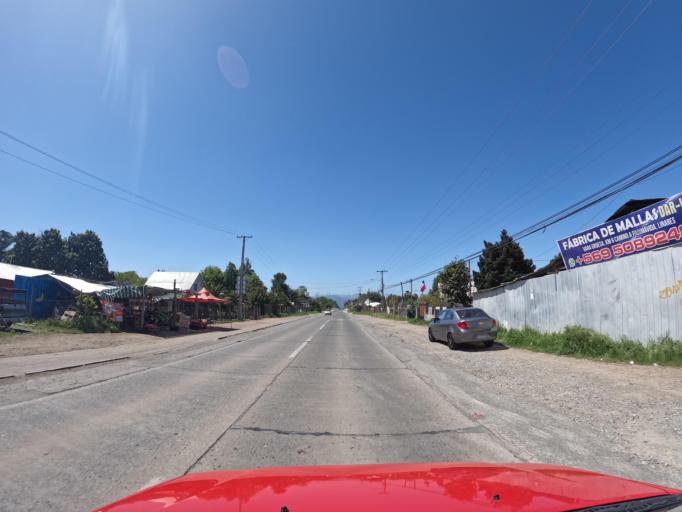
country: CL
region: Maule
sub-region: Provincia de Linares
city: Linares
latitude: -35.8324
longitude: -71.5297
